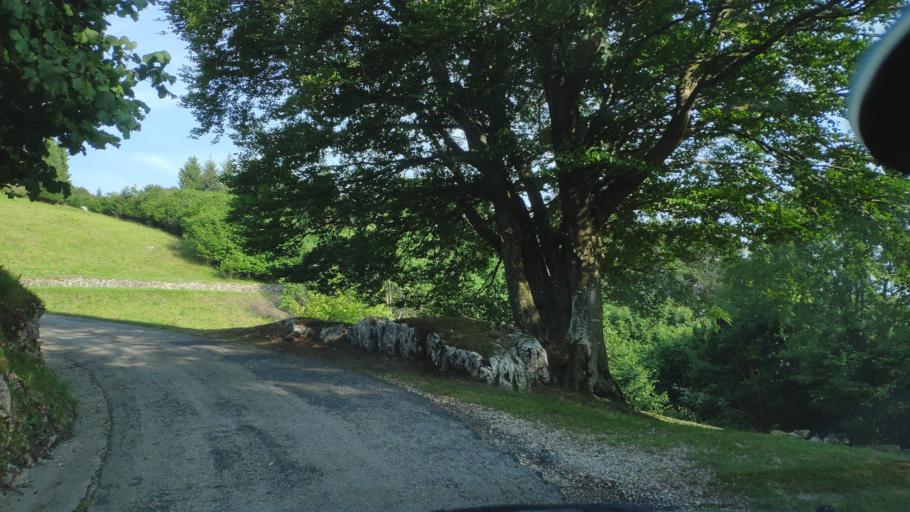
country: IT
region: Veneto
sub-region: Provincia di Vicenza
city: Cogollo del Cengio
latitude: 45.8078
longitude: 11.4337
